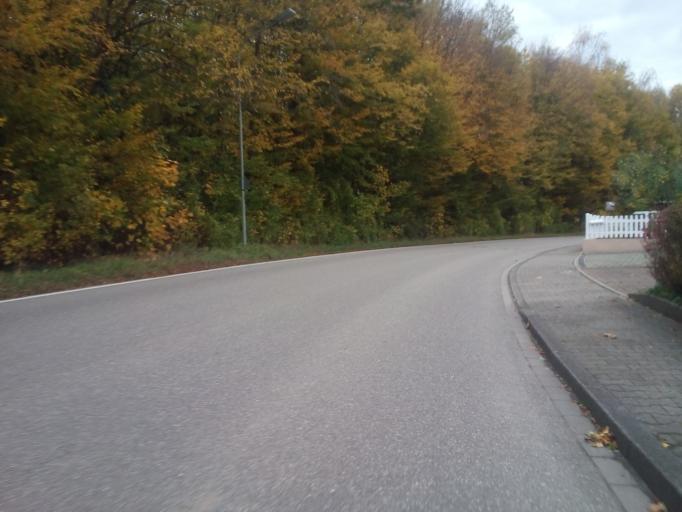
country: DE
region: Baden-Wuerttemberg
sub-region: Karlsruhe Region
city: Rheinmuenster
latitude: 48.7547
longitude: 8.0105
